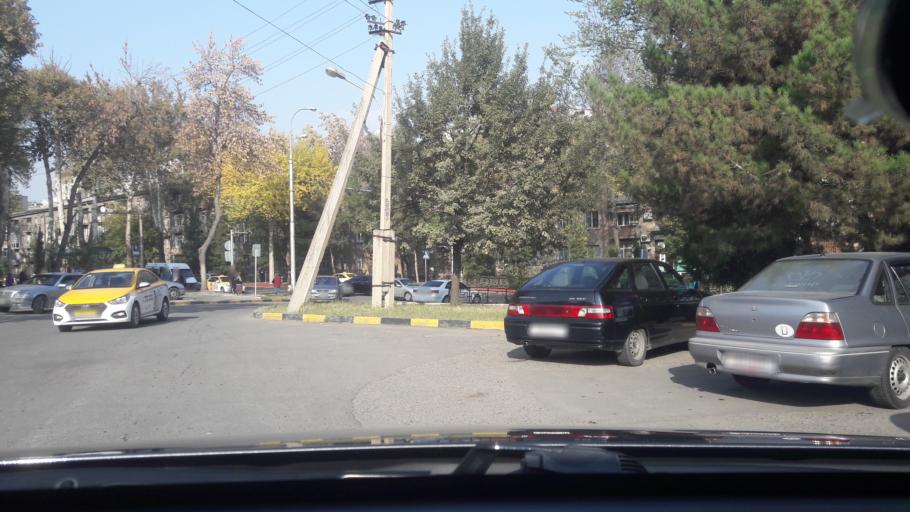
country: TJ
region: Dushanbe
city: Dushanbe
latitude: 38.5630
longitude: 68.7850
